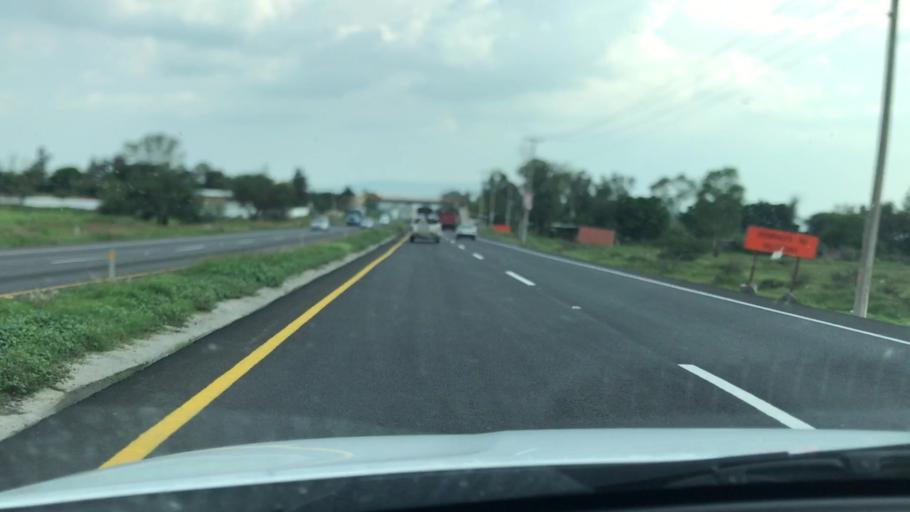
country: MX
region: Guanajuato
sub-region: Irapuato
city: San Ignacio de Rivera (Ojo de Agua)
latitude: 20.5411
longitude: -101.4564
